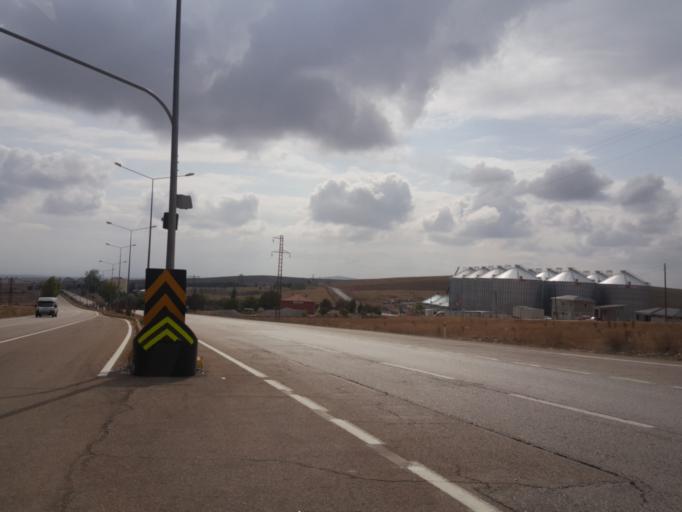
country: TR
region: Kirikkale
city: Keskin
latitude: 39.6561
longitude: 33.6173
